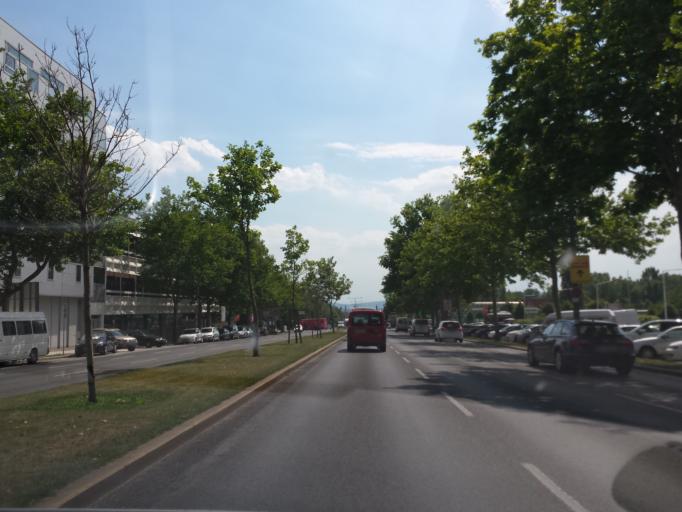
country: AT
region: Lower Austria
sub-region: Politischer Bezirk Modling
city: Vosendorf
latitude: 48.1672
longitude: 16.3483
